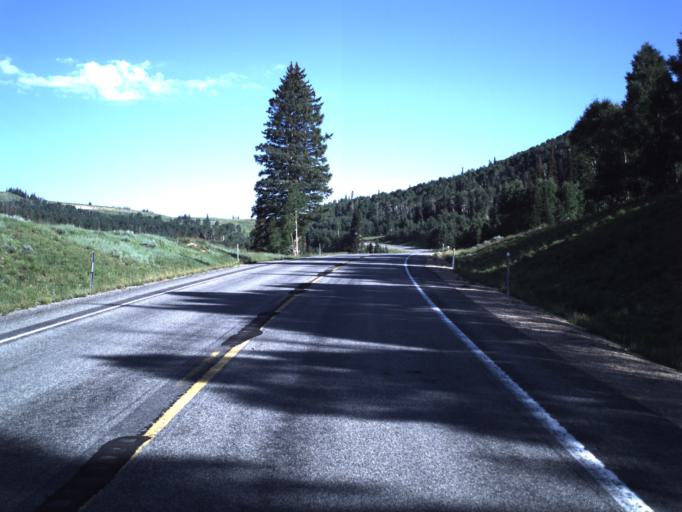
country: US
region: Utah
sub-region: Sanpete County
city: Fairview
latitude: 39.6002
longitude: -111.2725
